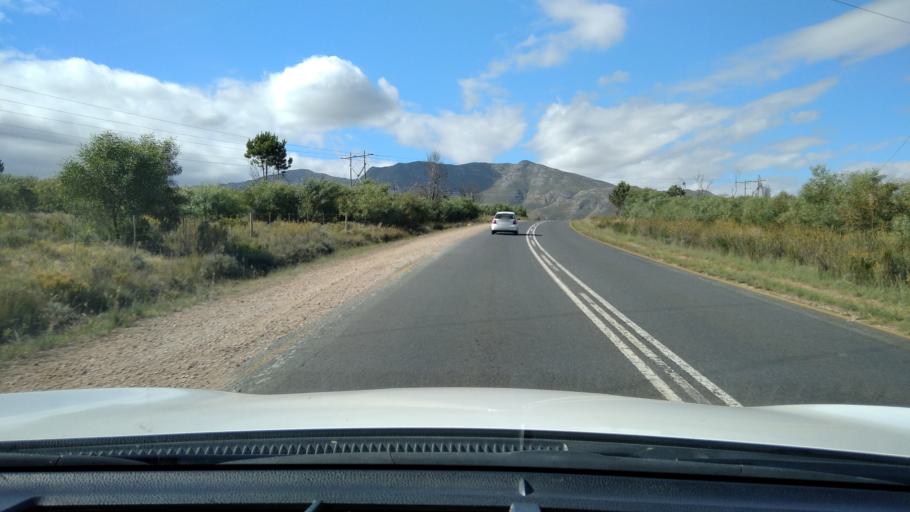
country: ZA
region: Western Cape
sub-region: Overberg District Municipality
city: Hermanus
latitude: -34.2415
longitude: 19.1848
